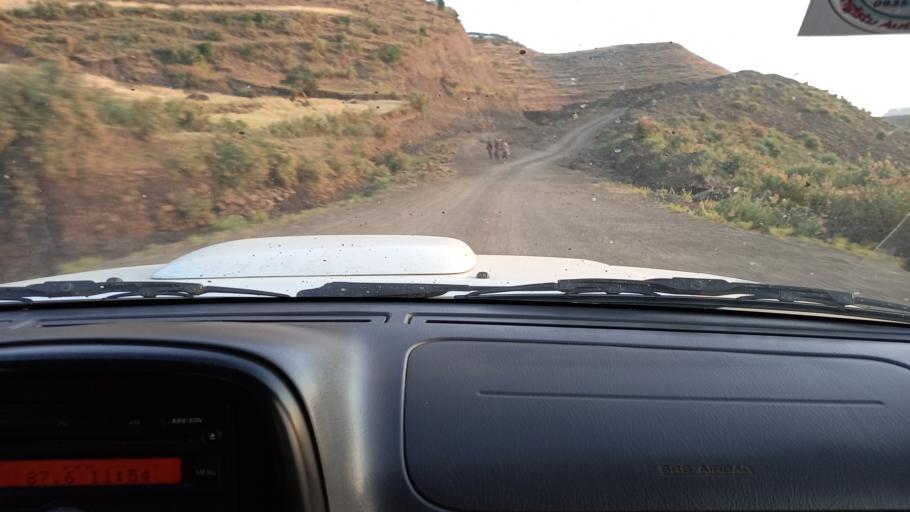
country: ET
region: Amhara
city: Debark'
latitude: 13.0520
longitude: 38.0197
